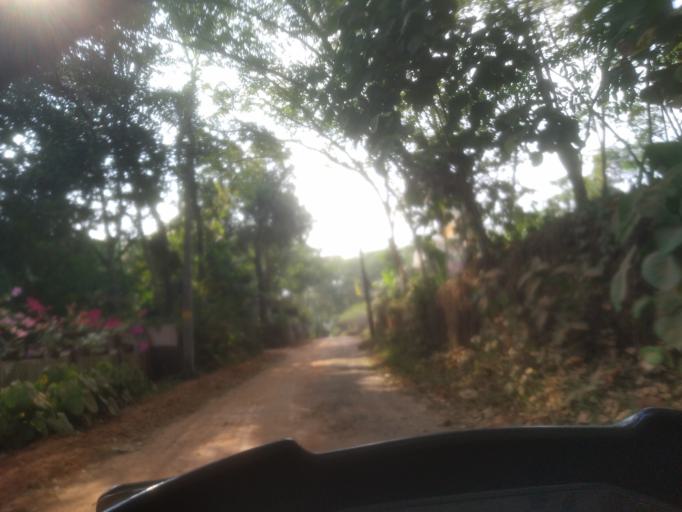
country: IN
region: Kerala
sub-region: Ernakulam
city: Piravam
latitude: 9.8770
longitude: 76.5497
